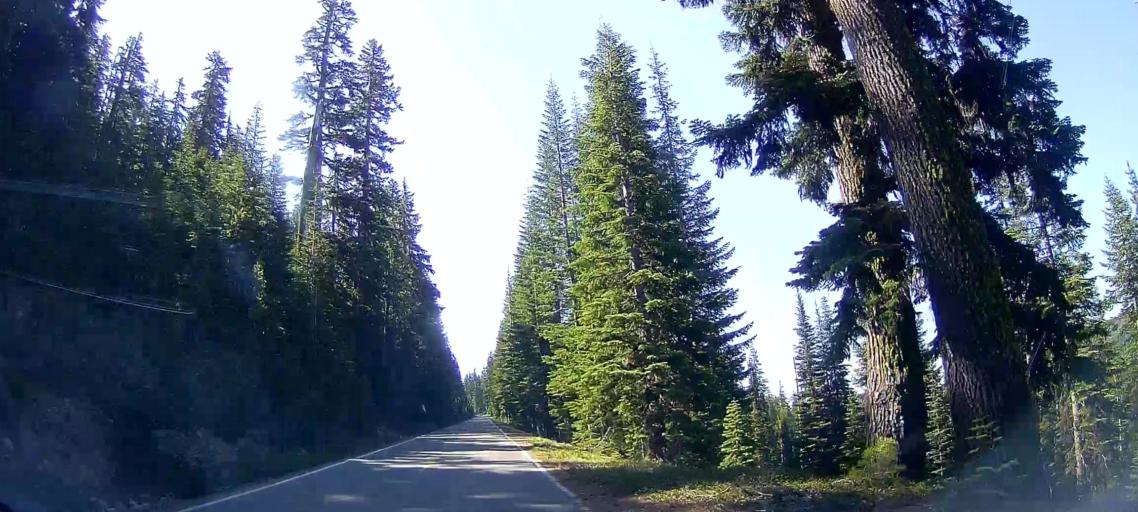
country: US
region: Oregon
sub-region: Jackson County
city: Shady Cove
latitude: 42.8866
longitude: -122.1306
